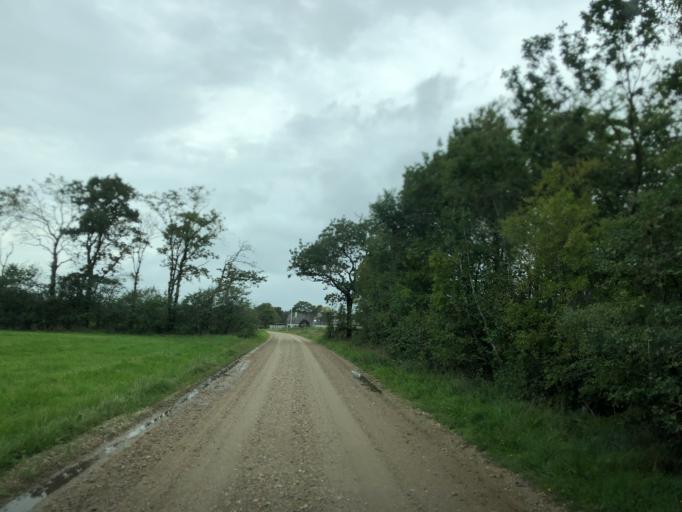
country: DK
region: Central Jutland
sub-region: Holstebro Kommune
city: Holstebro
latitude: 56.2376
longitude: 8.5217
